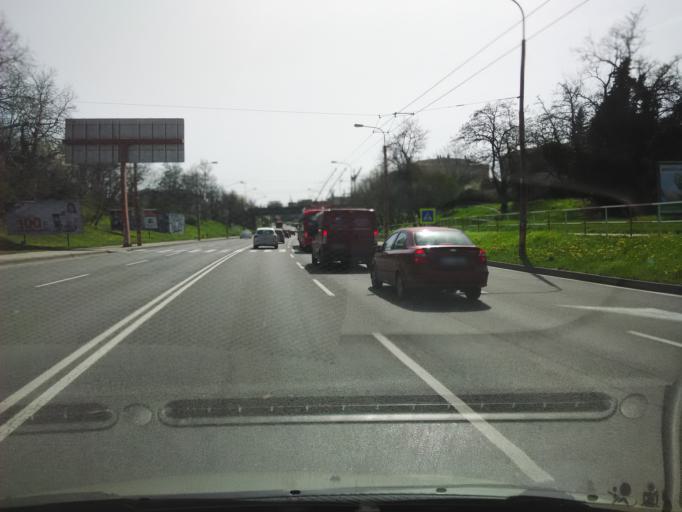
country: SK
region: Bratislavsky
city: Bratislava
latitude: 48.1472
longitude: 17.1849
